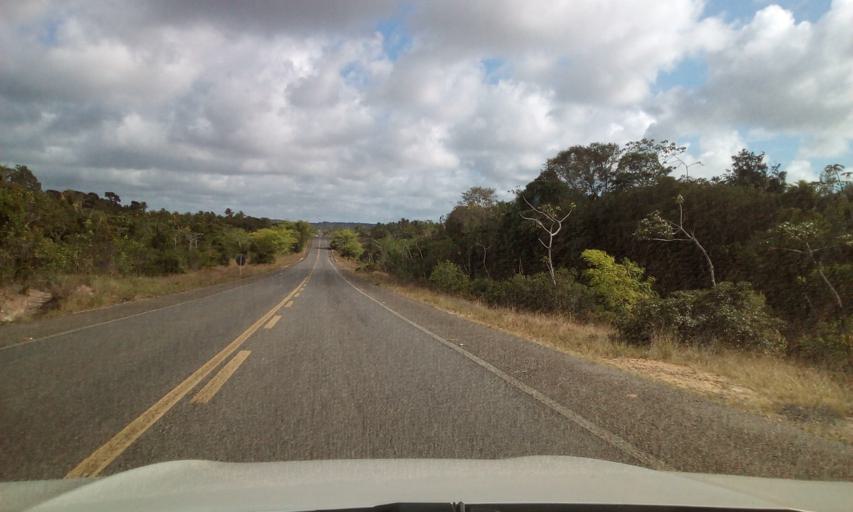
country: BR
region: Sergipe
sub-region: Indiaroba
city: Indiaroba
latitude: -11.6397
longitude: -37.5408
